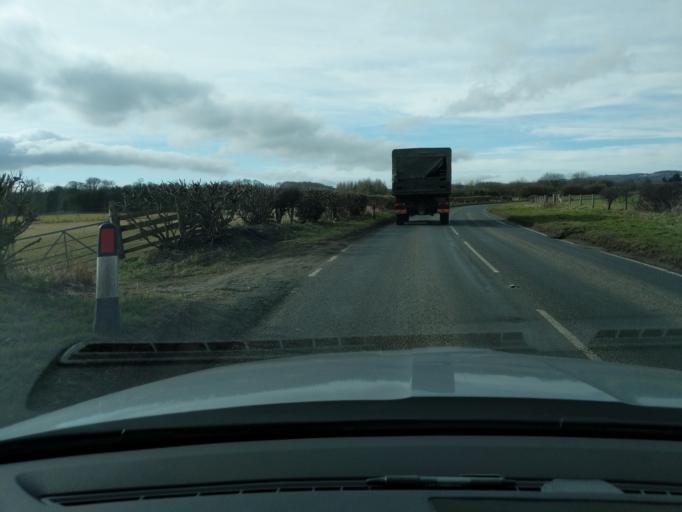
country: GB
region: England
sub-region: North Yorkshire
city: Catterick Garrison
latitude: 54.3941
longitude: -1.6788
